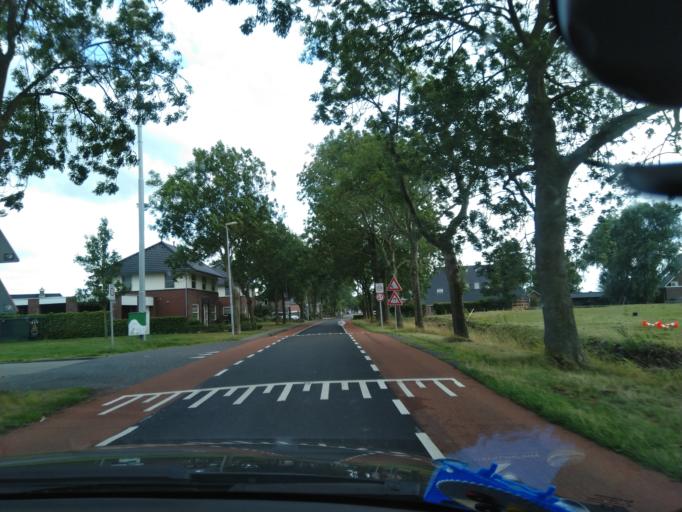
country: NL
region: Groningen
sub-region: Gemeente Zuidhorn
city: Aduard
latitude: 53.2298
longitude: 6.5001
